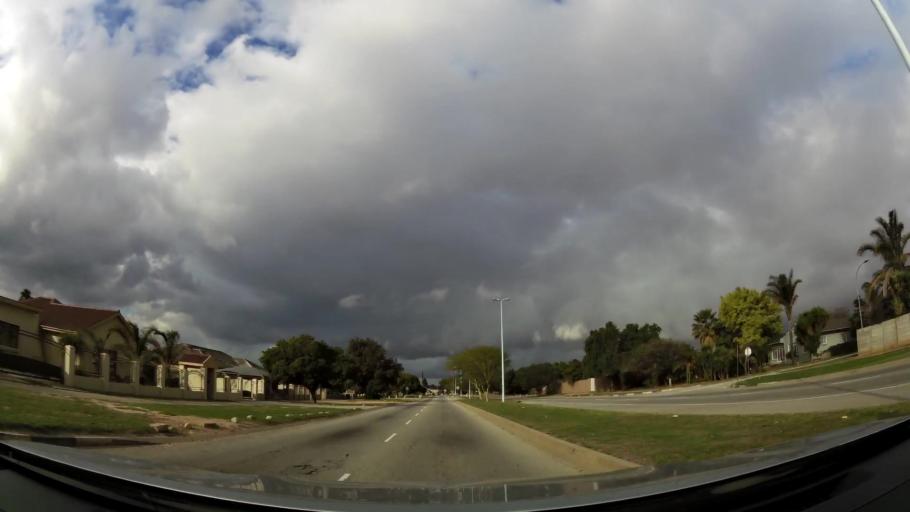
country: ZA
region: Eastern Cape
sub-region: Nelson Mandela Bay Metropolitan Municipality
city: Uitenhage
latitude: -33.8003
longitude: 25.4590
